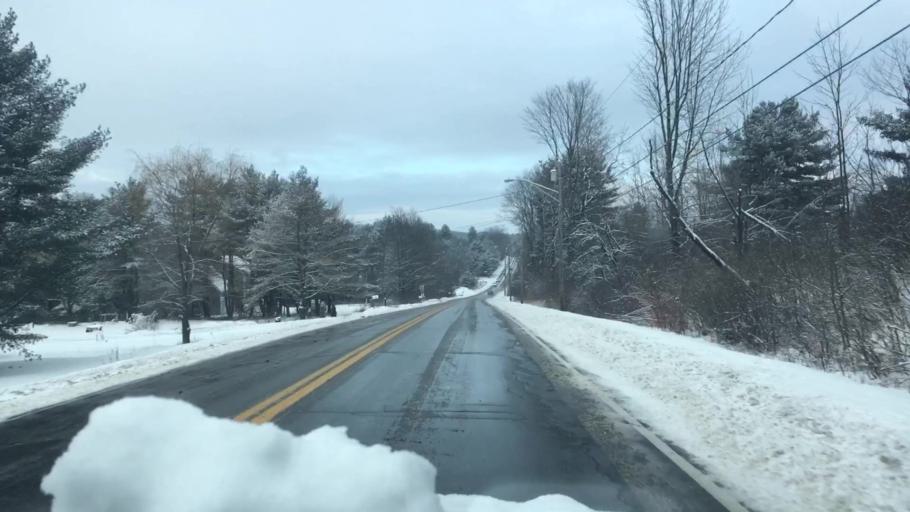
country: US
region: Maine
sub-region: Cumberland County
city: Westbrook
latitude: 43.7006
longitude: -70.3751
